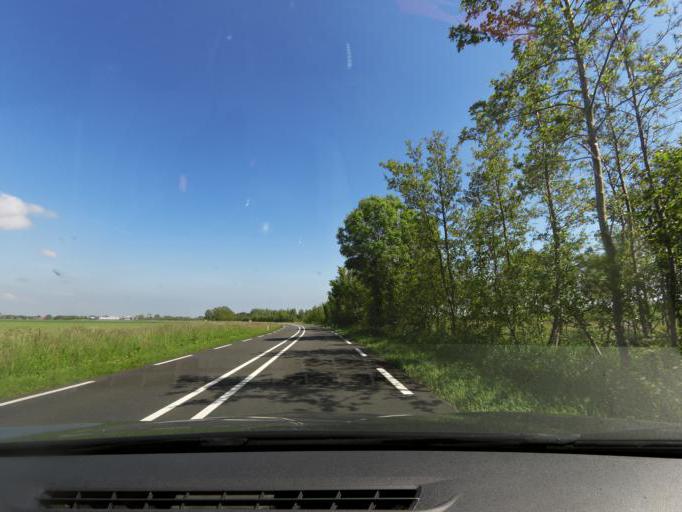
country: NL
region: South Holland
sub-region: Gemeente Hellevoetsluis
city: Nieuw-Helvoet
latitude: 51.8327
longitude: 4.0991
